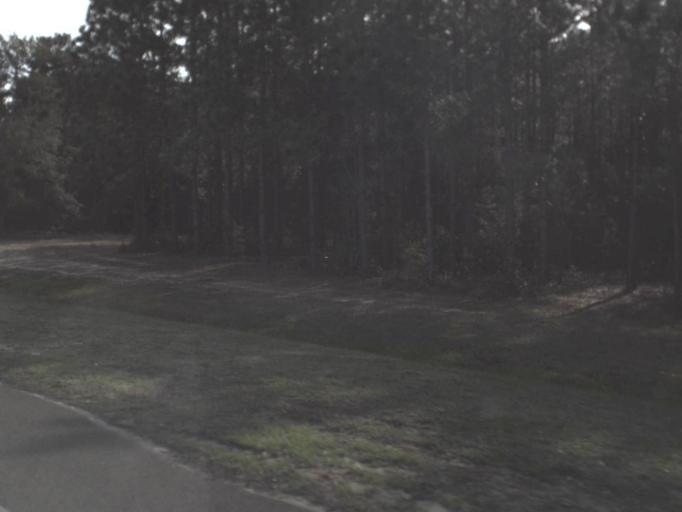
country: US
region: Florida
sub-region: Bay County
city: Tyndall Air Force Base
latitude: 30.0924
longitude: -85.6114
